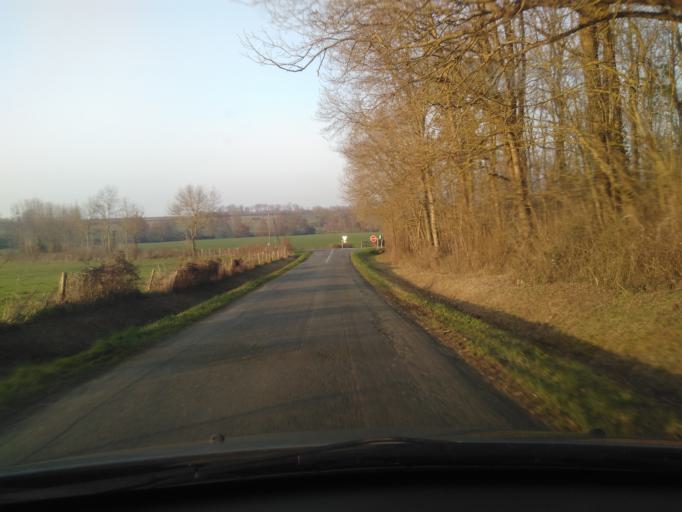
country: FR
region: Pays de la Loire
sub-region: Departement de la Vendee
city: Chantonnay
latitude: 46.6612
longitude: -1.0009
